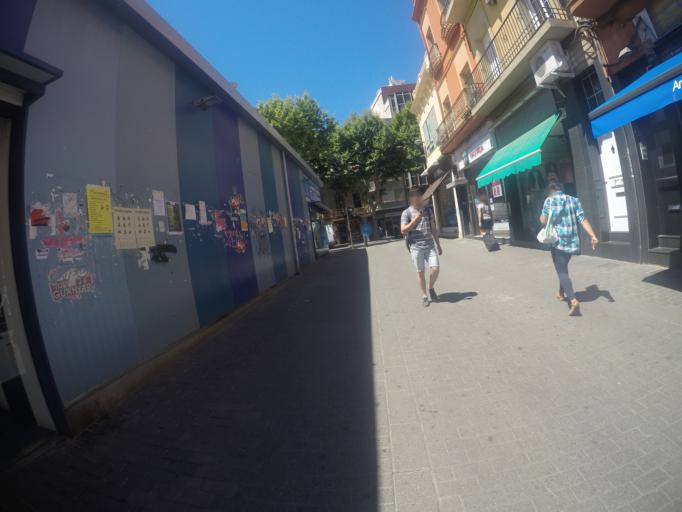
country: ES
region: Catalonia
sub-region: Provincia de Barcelona
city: Badalona
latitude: 41.4441
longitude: 2.2426
